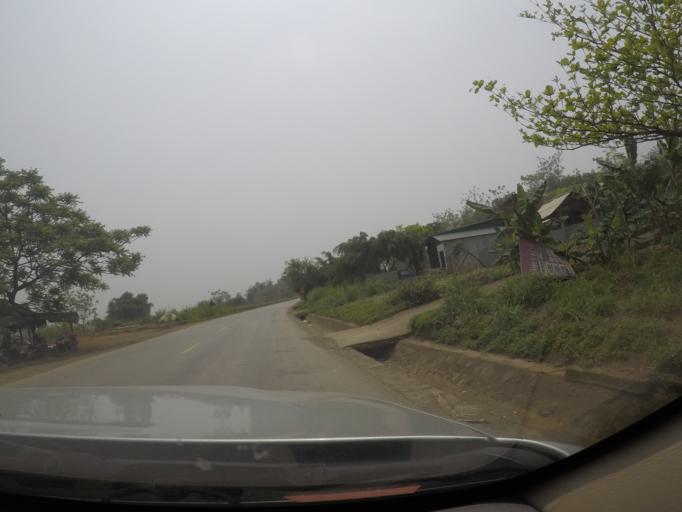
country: VN
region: Thanh Hoa
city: Thi Tran Thuong Xuan
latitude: 19.9844
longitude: 105.4065
